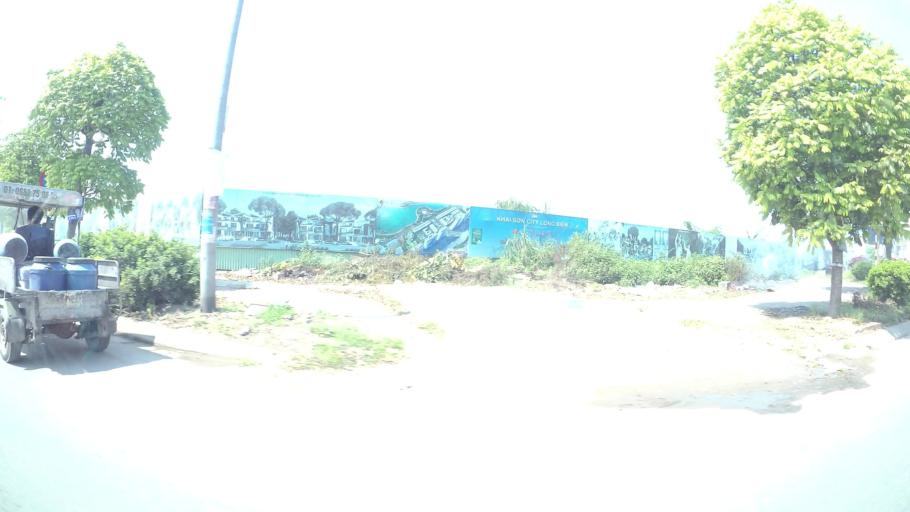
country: VN
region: Ha Noi
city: Hoan Kiem
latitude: 21.0618
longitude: 105.8820
